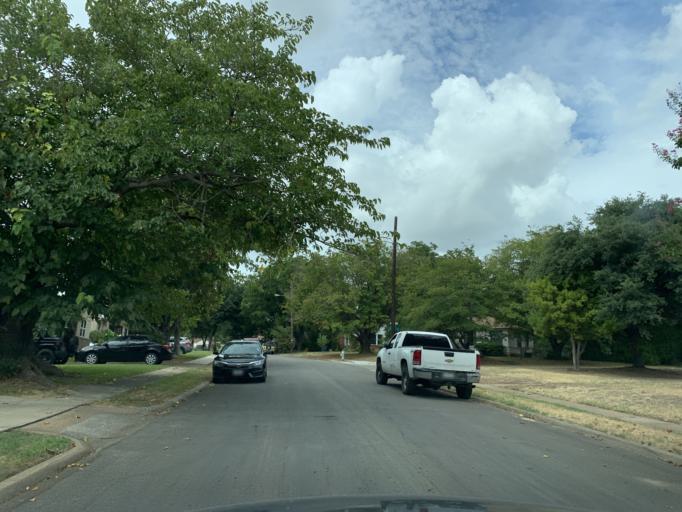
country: US
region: Texas
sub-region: Dallas County
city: Cockrell Hill
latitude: 32.7518
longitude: -96.8635
